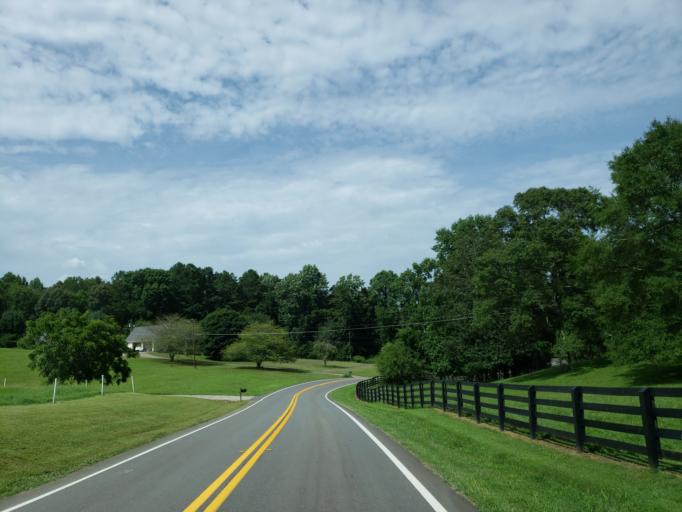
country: US
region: Georgia
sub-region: Cherokee County
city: Ball Ground
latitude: 34.3099
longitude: -84.4475
